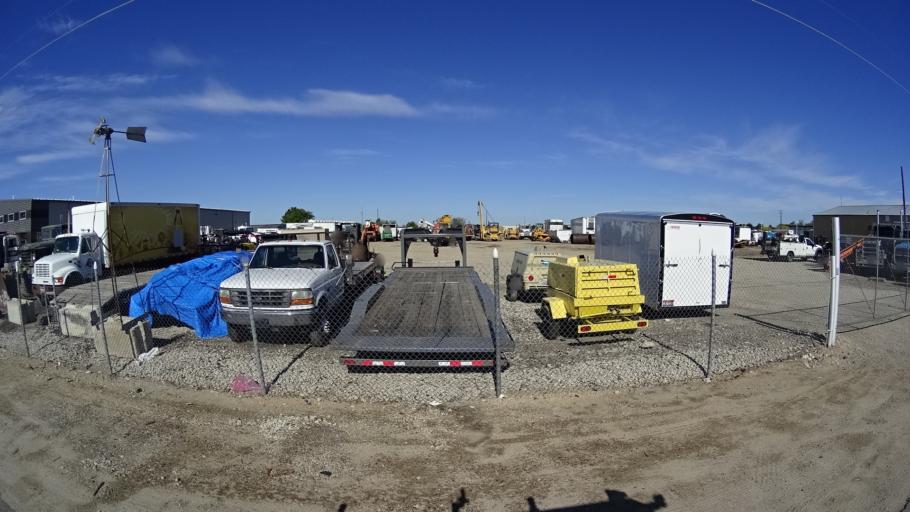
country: US
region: Idaho
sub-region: Ada County
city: Garden City
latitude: 43.5817
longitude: -116.2611
